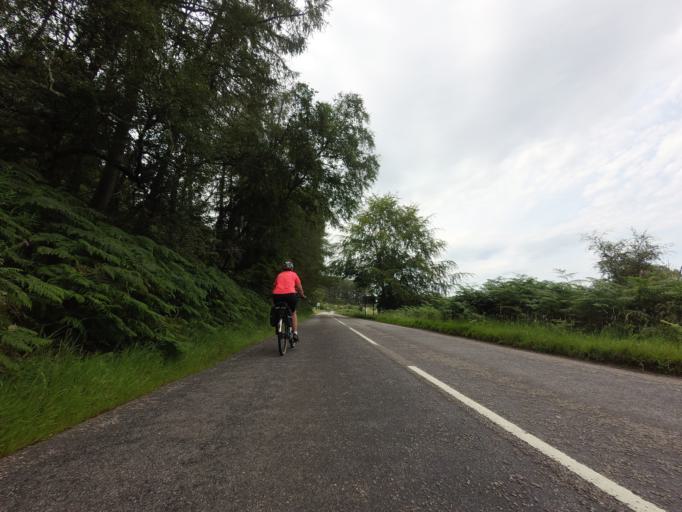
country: GB
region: Scotland
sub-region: Highland
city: Alness
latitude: 57.8529
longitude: -4.3020
